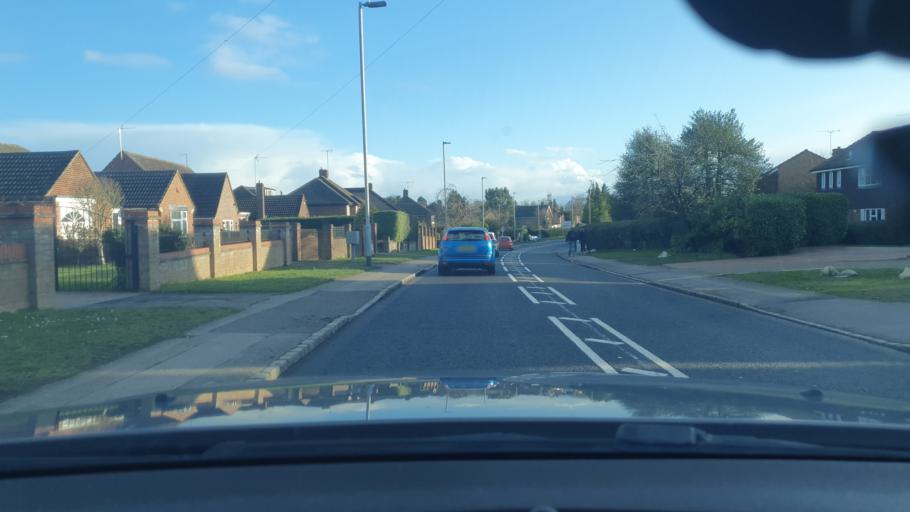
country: GB
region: England
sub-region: Wokingham
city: Woodley
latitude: 51.4571
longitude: -0.8984
